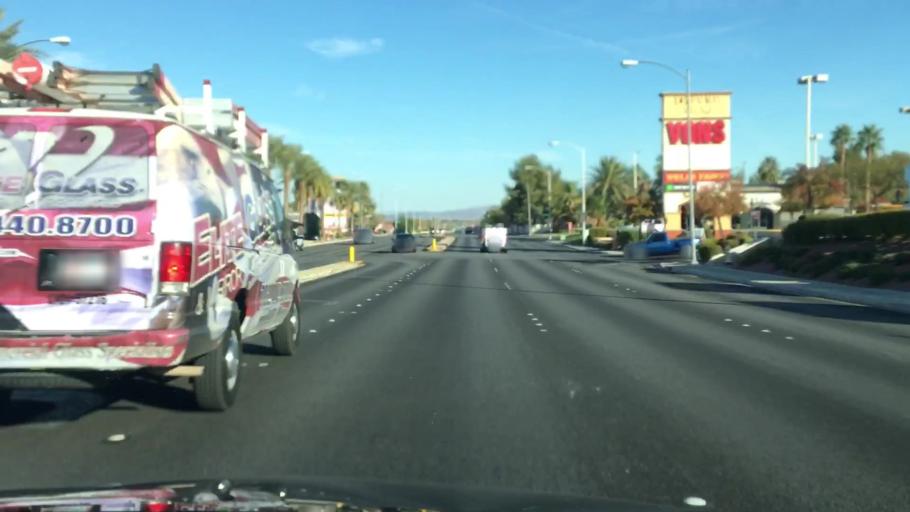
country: US
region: Nevada
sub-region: Clark County
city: Paradise
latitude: 36.0423
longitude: -115.1523
